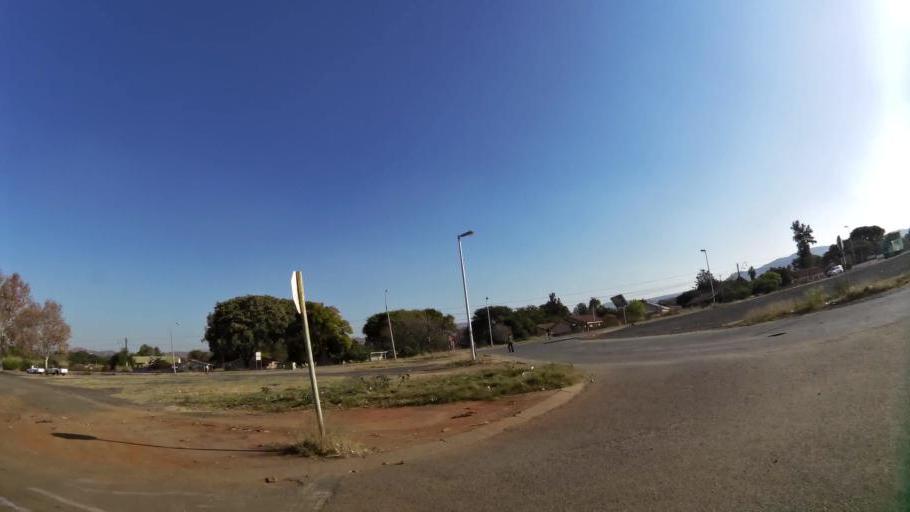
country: ZA
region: North-West
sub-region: Bojanala Platinum District Municipality
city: Rustenburg
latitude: -25.6511
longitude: 27.2406
